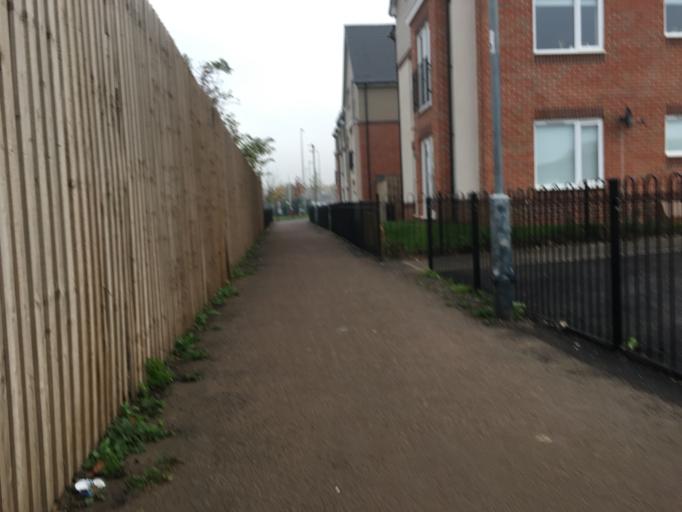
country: GB
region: England
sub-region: Warwickshire
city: Rugby
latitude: 52.3825
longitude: -1.2572
